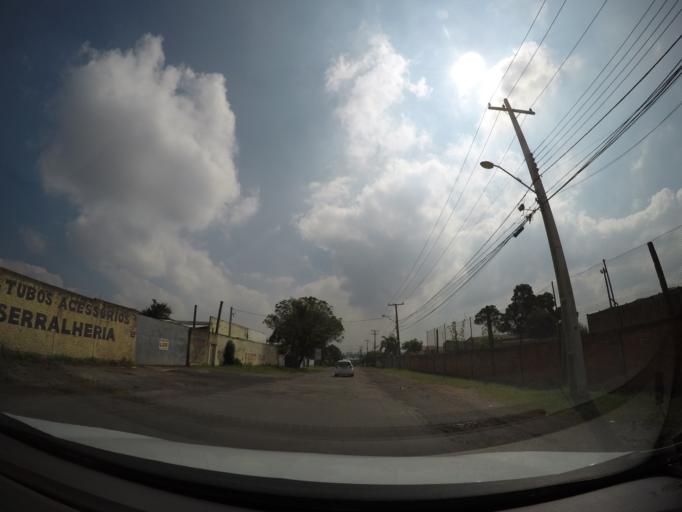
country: BR
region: Parana
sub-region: Curitiba
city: Curitiba
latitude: -25.4807
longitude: -49.2602
